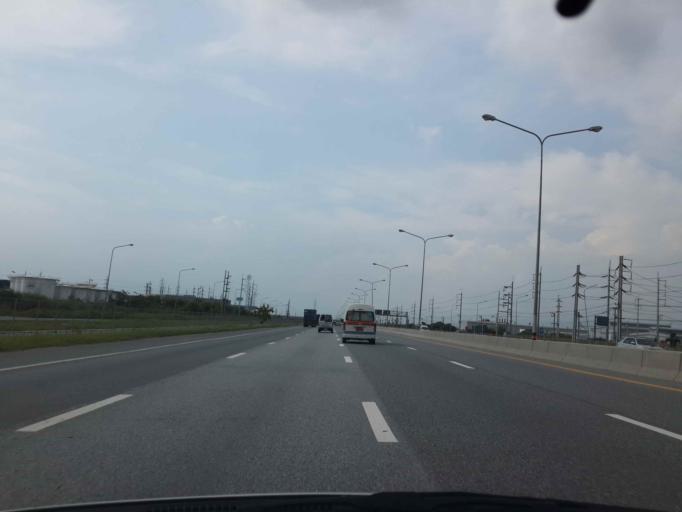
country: TH
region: Chon Buri
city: Phan Thong
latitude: 13.4319
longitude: 101.0464
